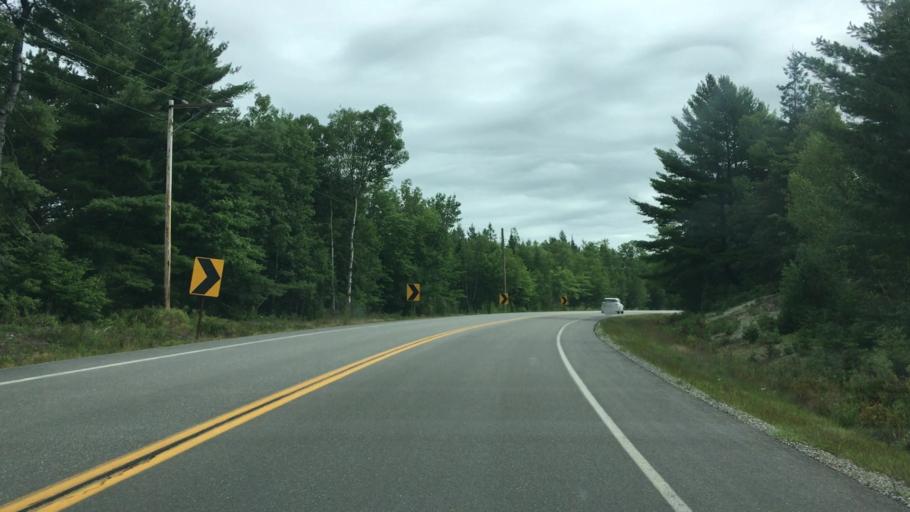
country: US
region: Maine
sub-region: Washington County
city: Machias
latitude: 45.0008
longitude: -67.5820
